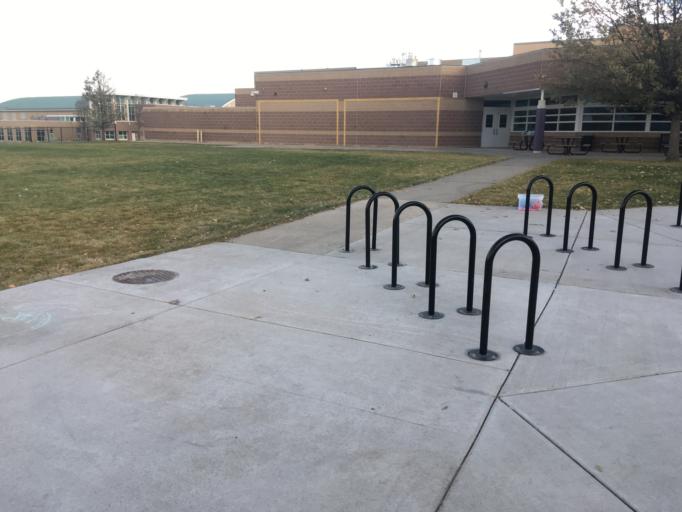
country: US
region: Colorado
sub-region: Boulder County
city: Superior
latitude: 39.9522
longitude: -105.1441
